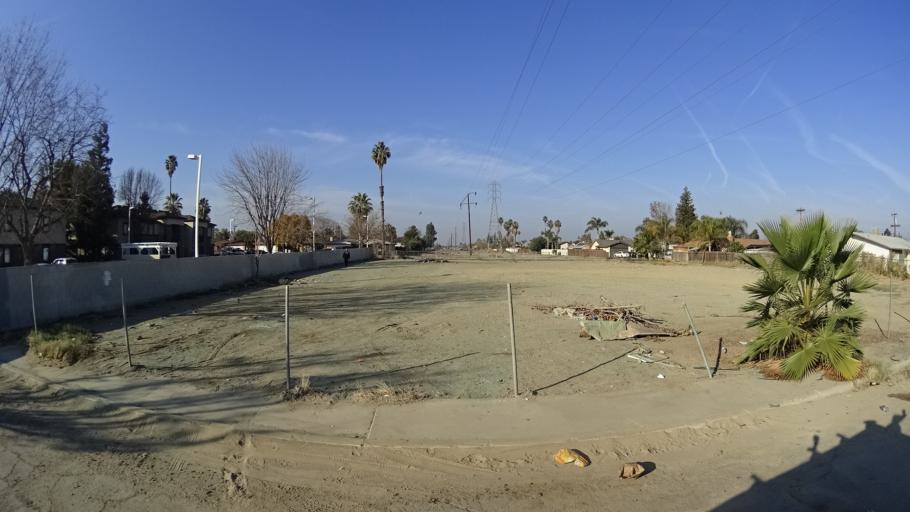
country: US
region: California
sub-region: Kern County
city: Greenfield
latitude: 35.3118
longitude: -119.0065
